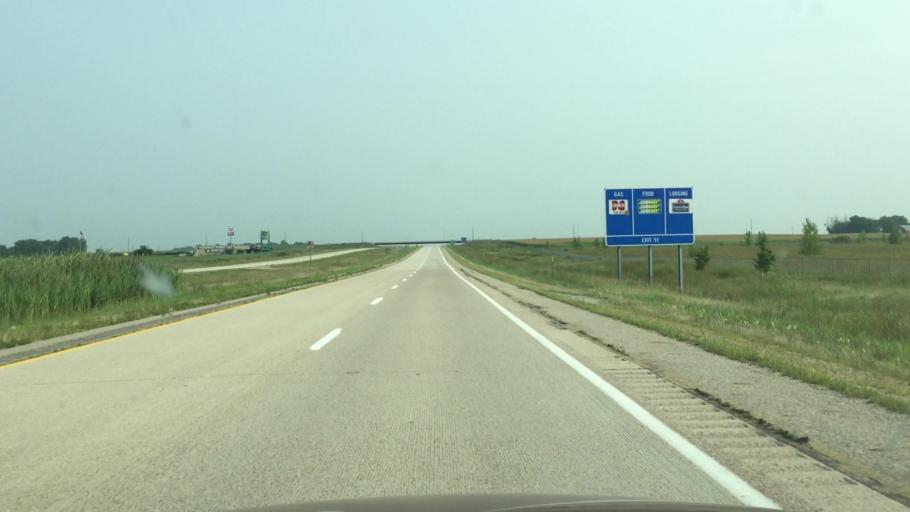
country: US
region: Iowa
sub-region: Osceola County
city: Sibley
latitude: 43.3968
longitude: -95.7169
